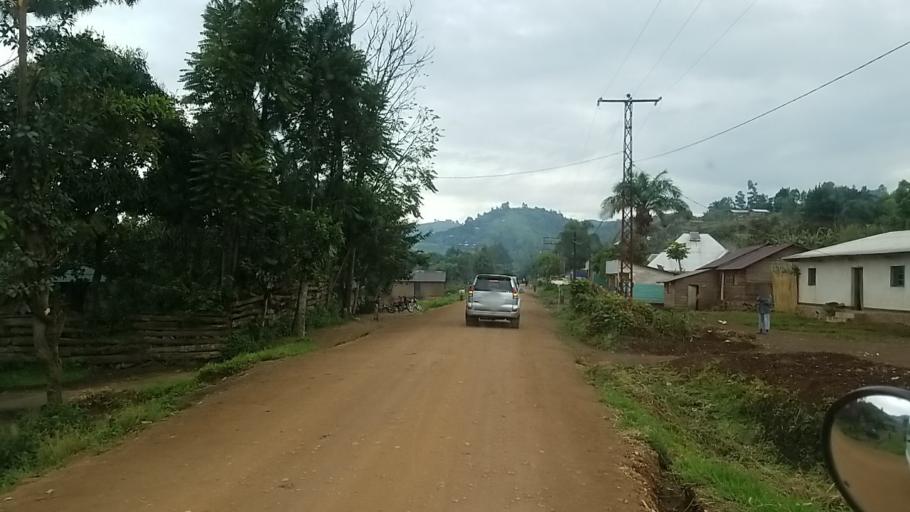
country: CD
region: Nord Kivu
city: Sake
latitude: -1.6941
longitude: 29.0154
